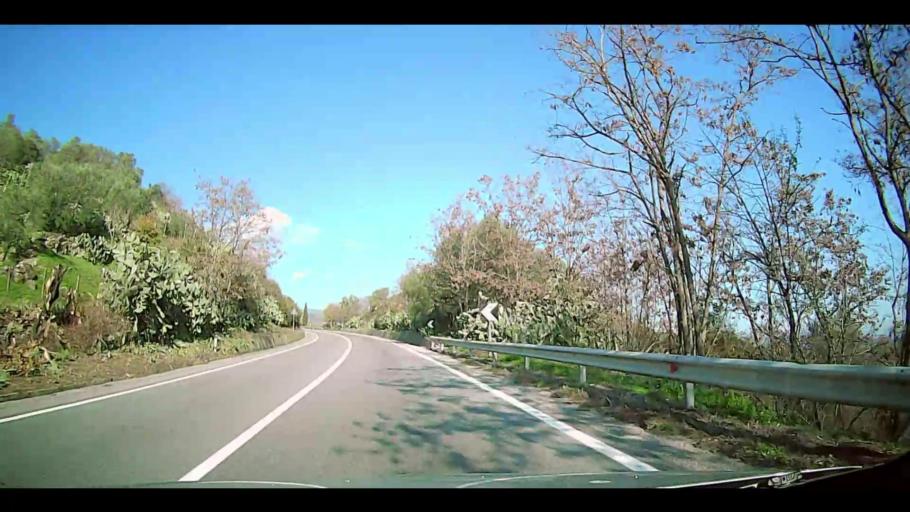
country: IT
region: Calabria
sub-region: Provincia di Crotone
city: Caccuri
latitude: 39.2007
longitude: 16.8117
